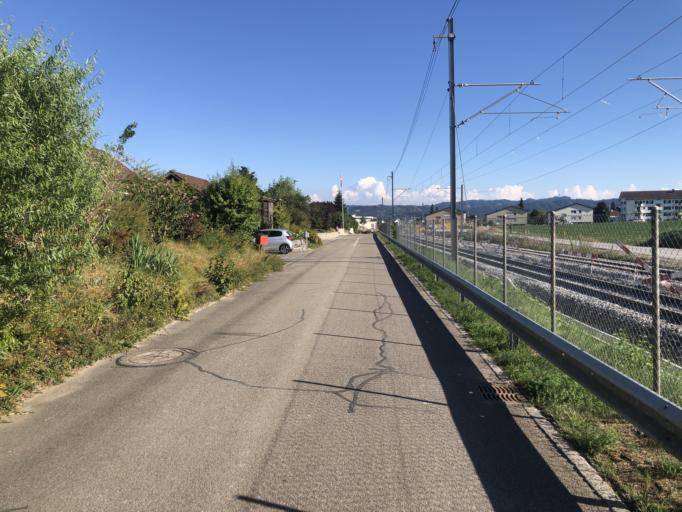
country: CH
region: Bern
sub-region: Bern-Mittelland District
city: Jegenstorf
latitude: 47.0582
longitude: 7.5089
